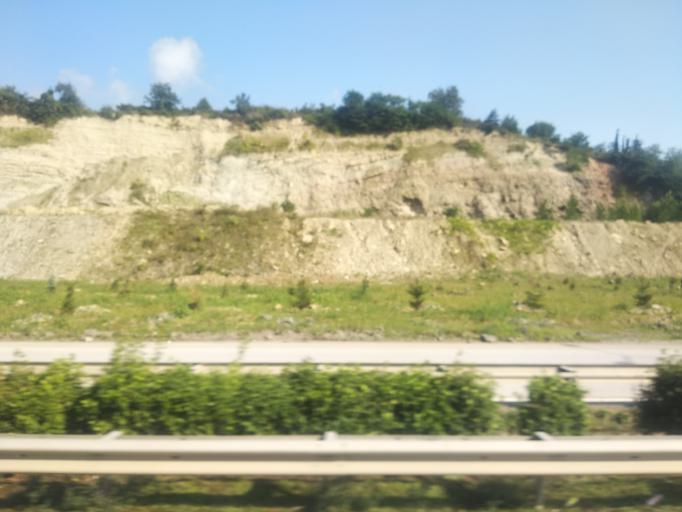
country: TR
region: Ordu
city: Ordu
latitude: 41.0007
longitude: 37.8231
